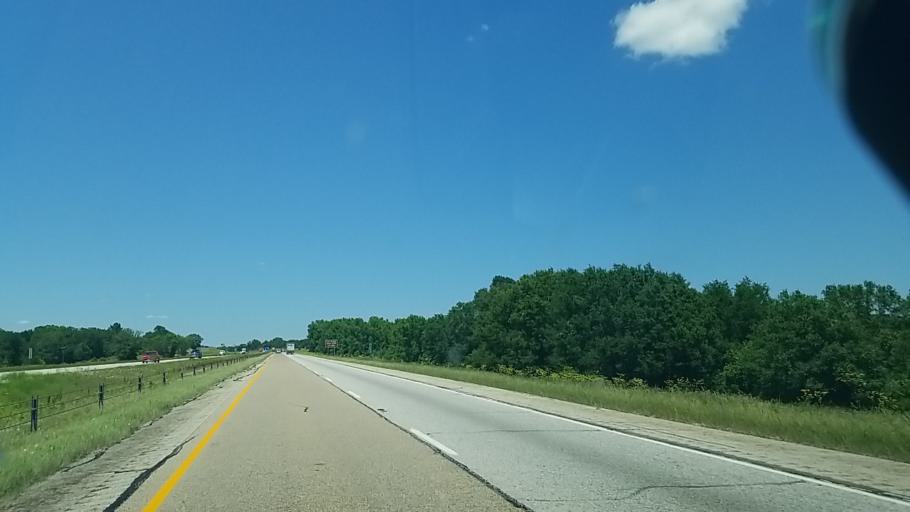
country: US
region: Texas
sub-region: Leon County
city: Centerville
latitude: 31.2421
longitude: -95.9914
